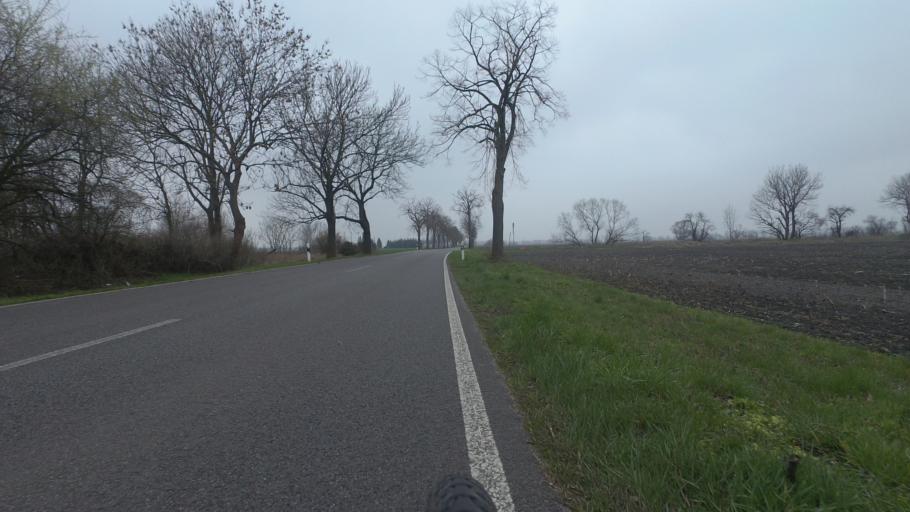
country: DE
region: Brandenburg
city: Nauen
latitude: 52.6211
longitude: 12.8690
